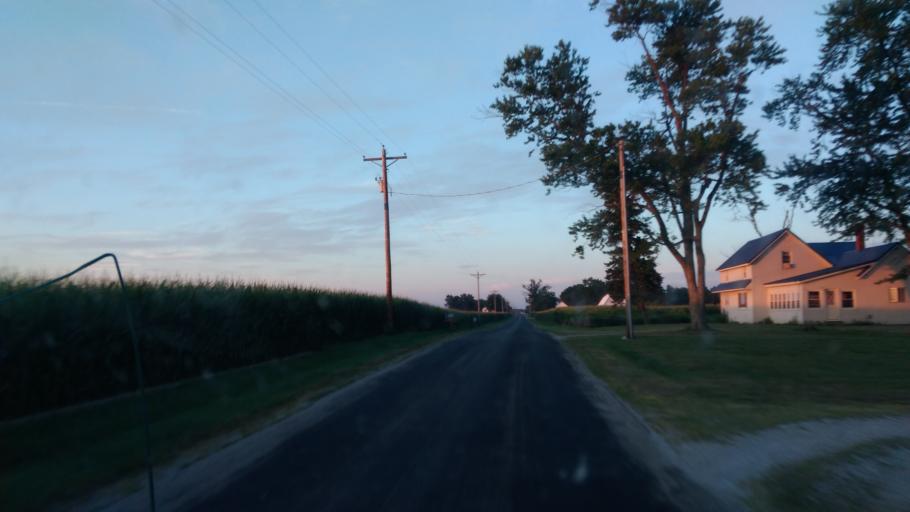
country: US
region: Indiana
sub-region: Wells County
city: Bluffton
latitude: 40.6781
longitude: -85.1074
